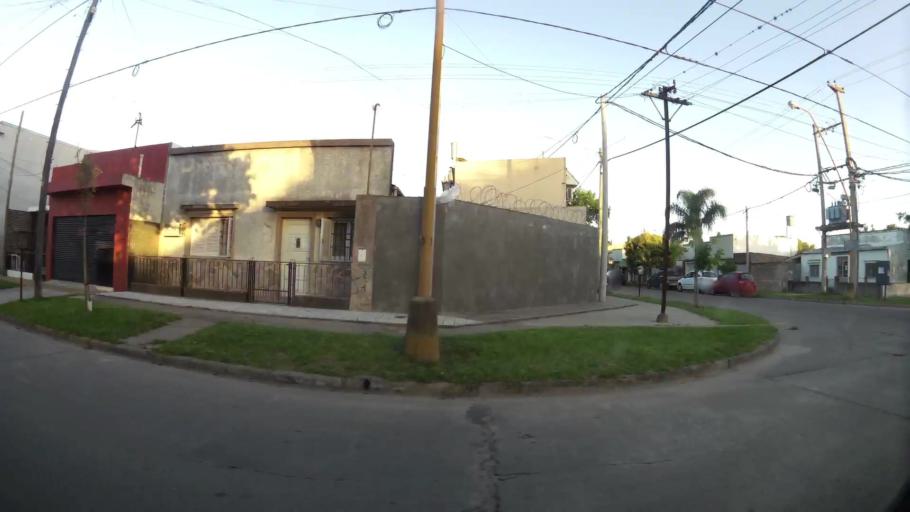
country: AR
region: Santa Fe
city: Santa Fe de la Vera Cruz
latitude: -31.6040
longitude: -60.6789
